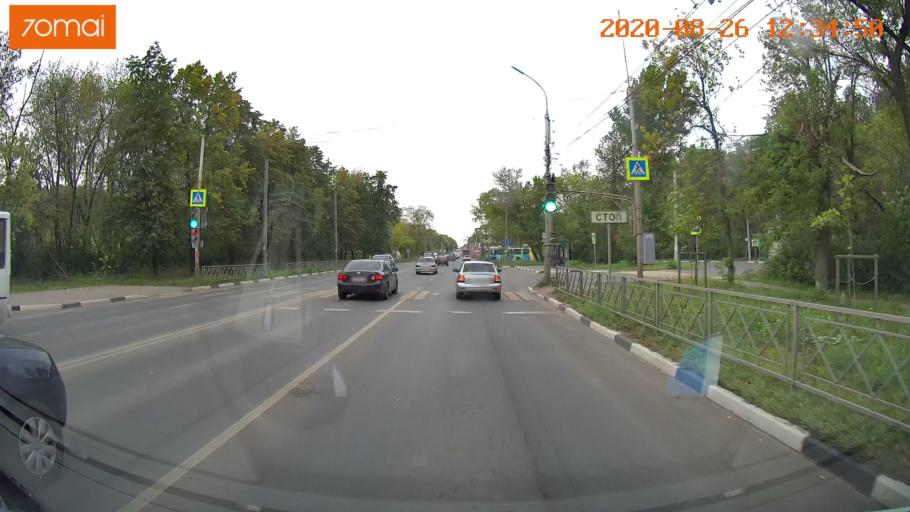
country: RU
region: Rjazan
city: Ryazan'
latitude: 54.5912
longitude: 39.7701
